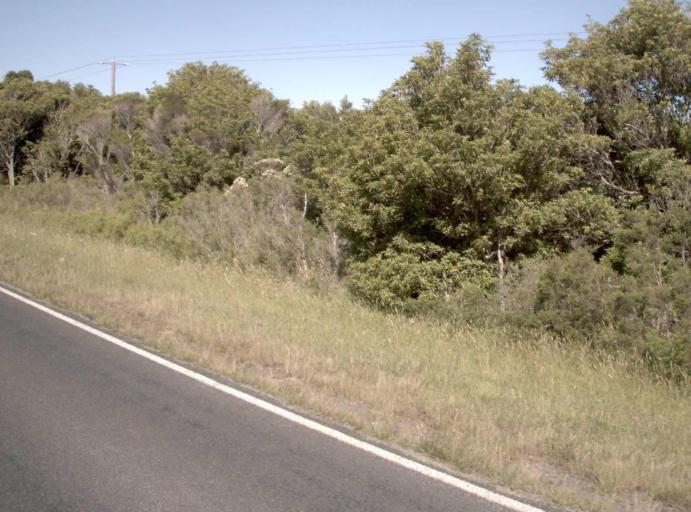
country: AU
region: Victoria
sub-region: Latrobe
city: Morwell
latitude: -38.6486
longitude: 146.4705
